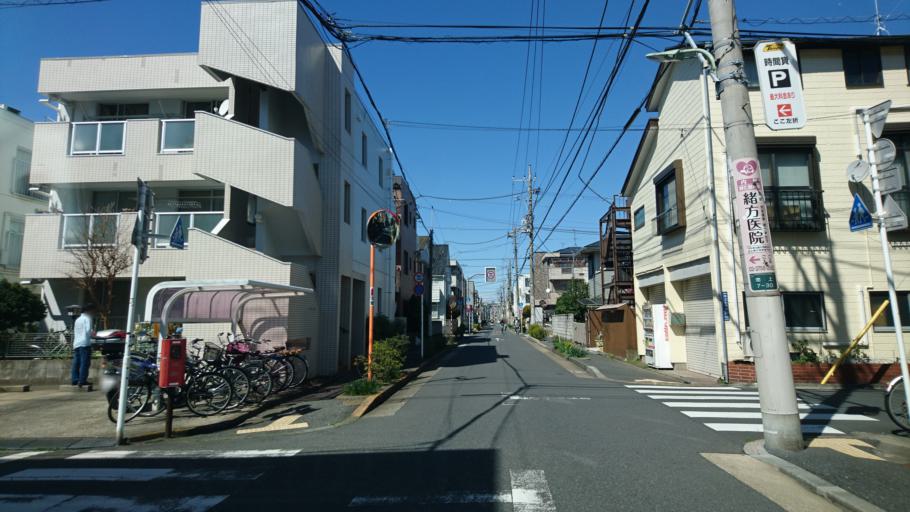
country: JP
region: Kanagawa
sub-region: Kawasaki-shi
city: Kawasaki
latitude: 35.5672
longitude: 139.7010
